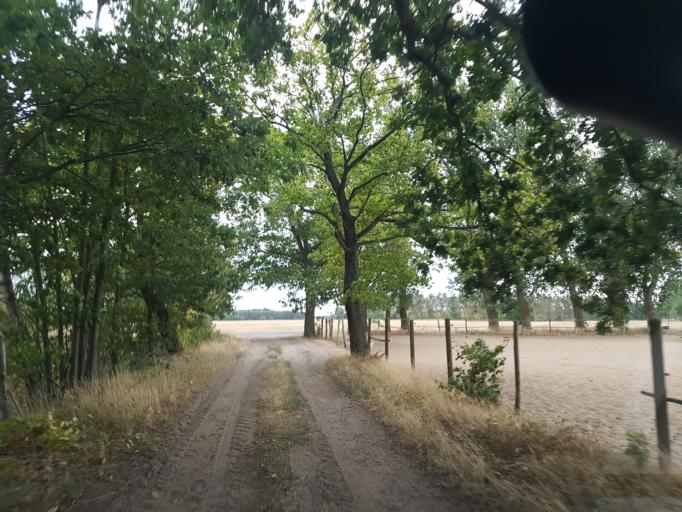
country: DE
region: Brandenburg
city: Schilda
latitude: 51.5700
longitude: 13.3469
